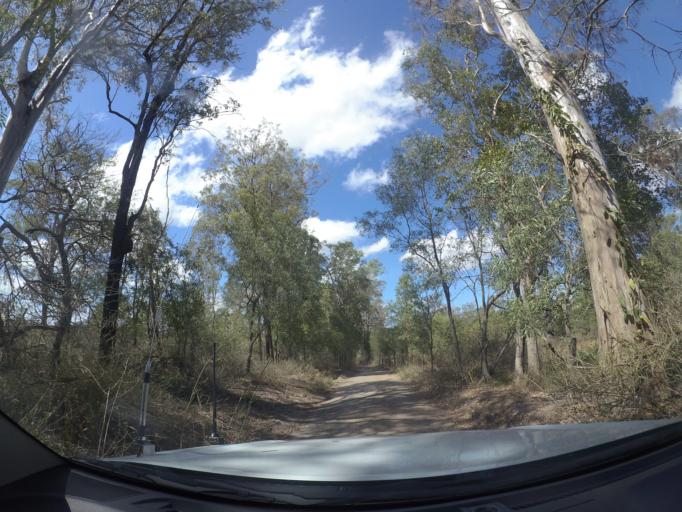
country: AU
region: Queensland
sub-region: Logan
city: Cedar Vale
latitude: -27.8423
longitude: 152.9739
